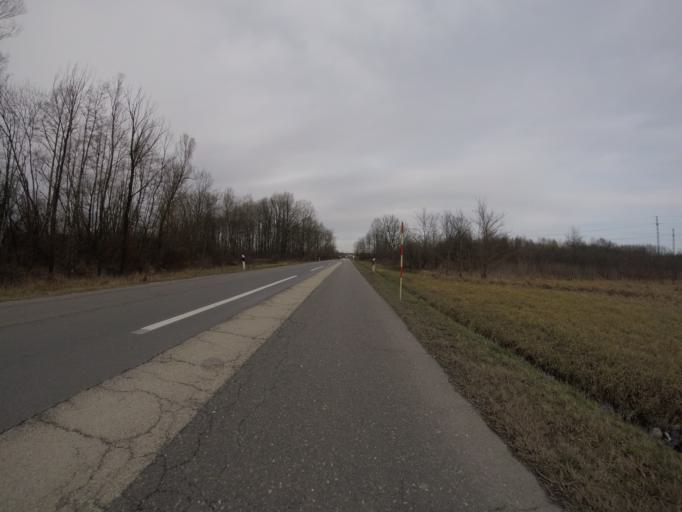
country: HR
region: Grad Zagreb
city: Horvati
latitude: 45.5624
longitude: 15.8622
